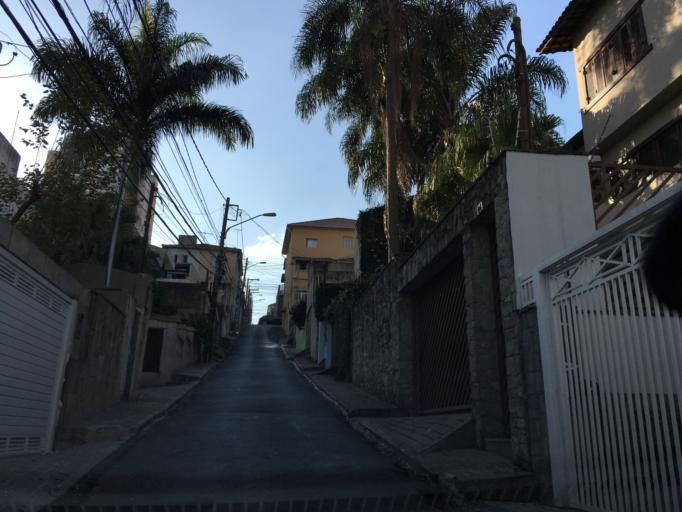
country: BR
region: Sao Paulo
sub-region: Sao Paulo
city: Sao Paulo
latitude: -23.5005
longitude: -46.6395
